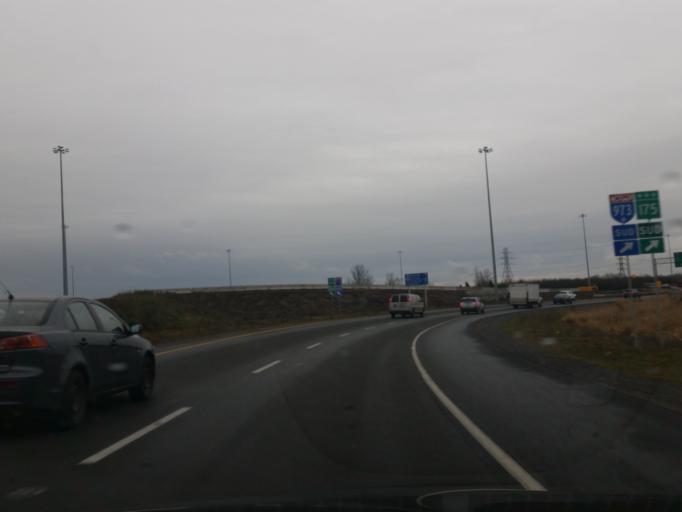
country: CA
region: Quebec
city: Quebec
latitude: 46.8352
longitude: -71.2678
